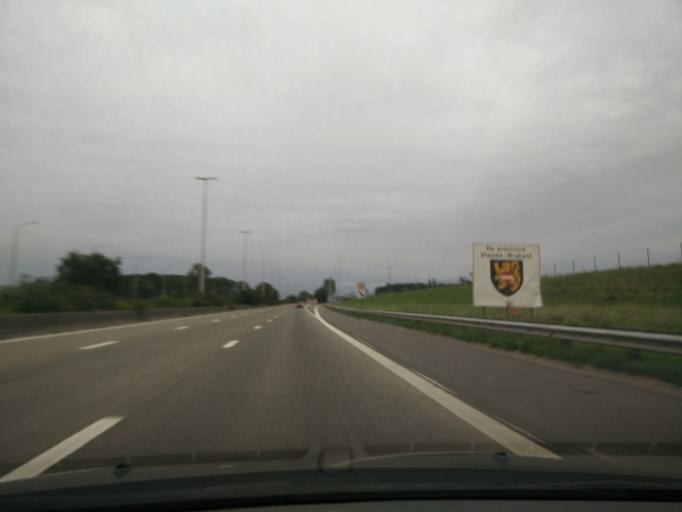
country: BE
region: Wallonia
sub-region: Province de Liege
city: Lincent
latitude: 50.7162
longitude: 5.0556
